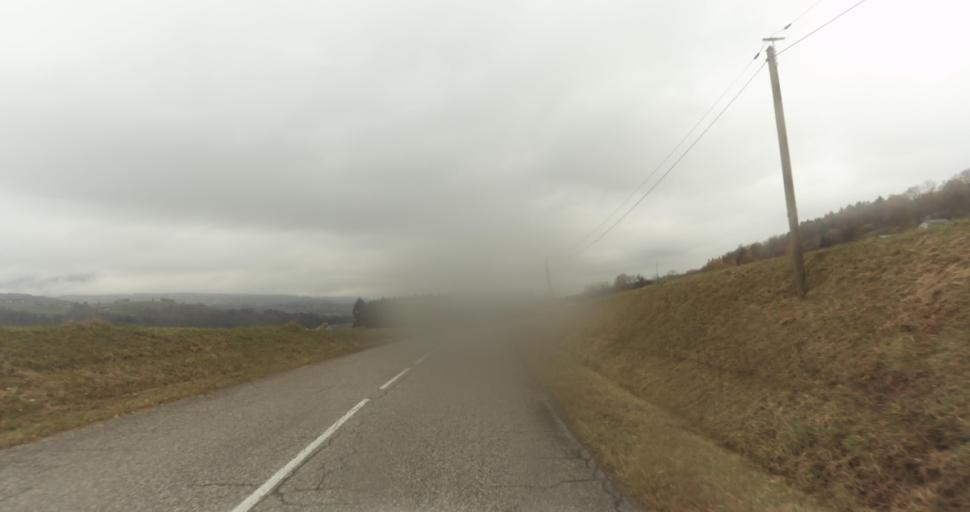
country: FR
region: Rhone-Alpes
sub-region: Departement de la Haute-Savoie
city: Saint-Martin-Bellevue
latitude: 45.9862
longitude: 6.1549
